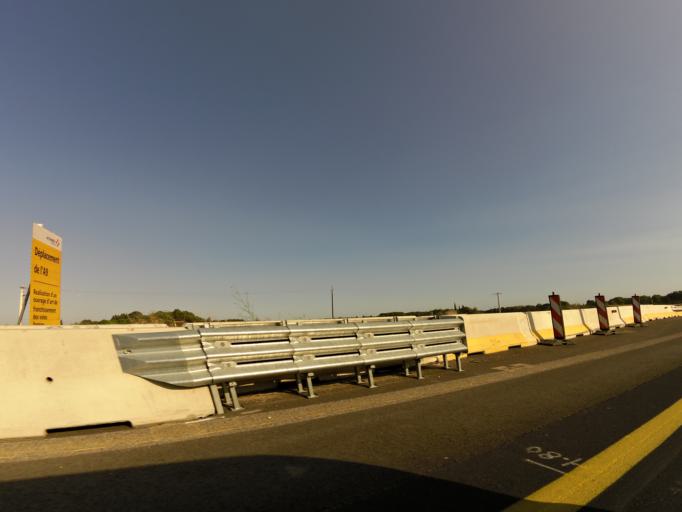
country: FR
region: Languedoc-Roussillon
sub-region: Departement de l'Herault
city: Saint-Aunes
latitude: 43.6303
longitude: 3.9675
